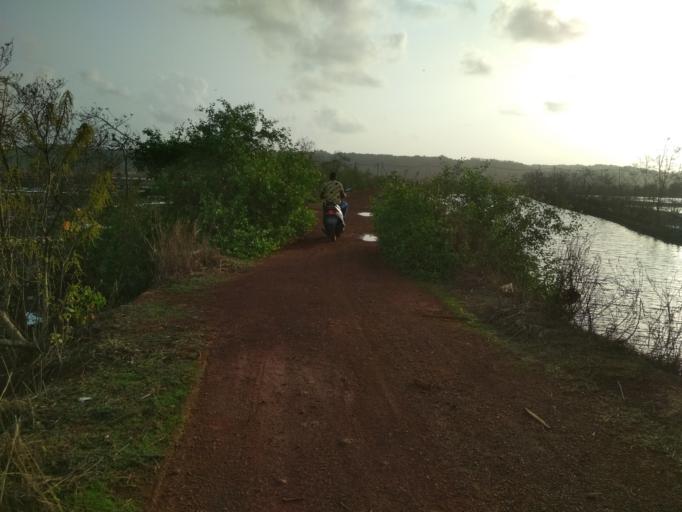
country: IN
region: Goa
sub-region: North Goa
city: Serula
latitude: 15.5290
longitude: 73.8594
